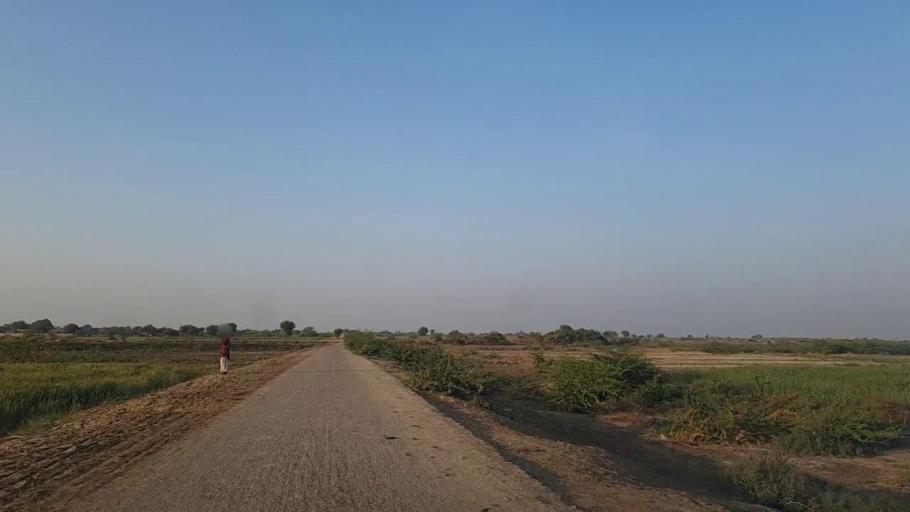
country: PK
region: Sindh
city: Naukot
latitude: 24.9567
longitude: 69.4521
